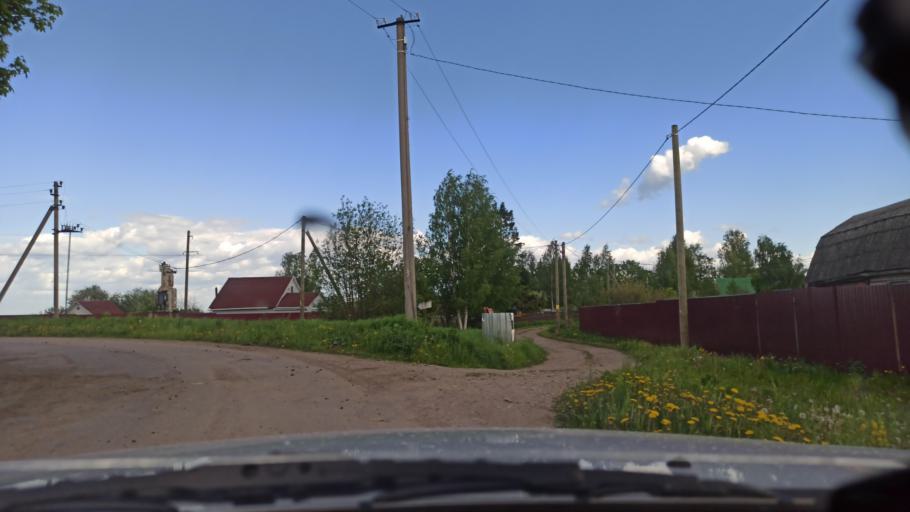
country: RU
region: Vologda
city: Vologda
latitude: 59.3293
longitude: 39.8383
